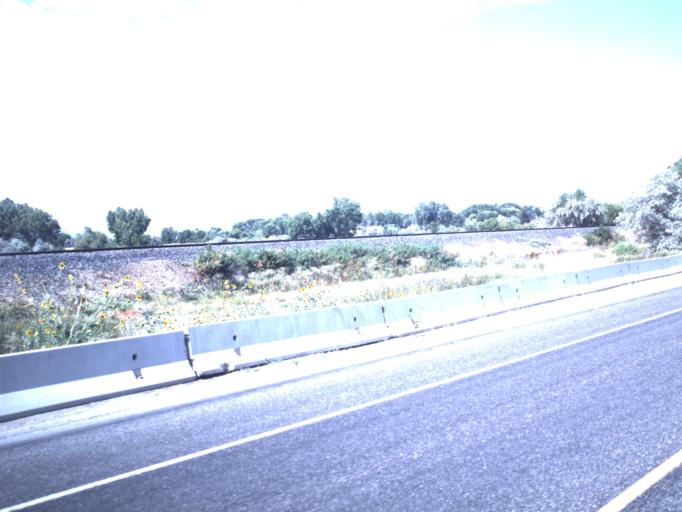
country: US
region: Utah
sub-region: Box Elder County
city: Brigham City
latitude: 41.5467
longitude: -112.0979
